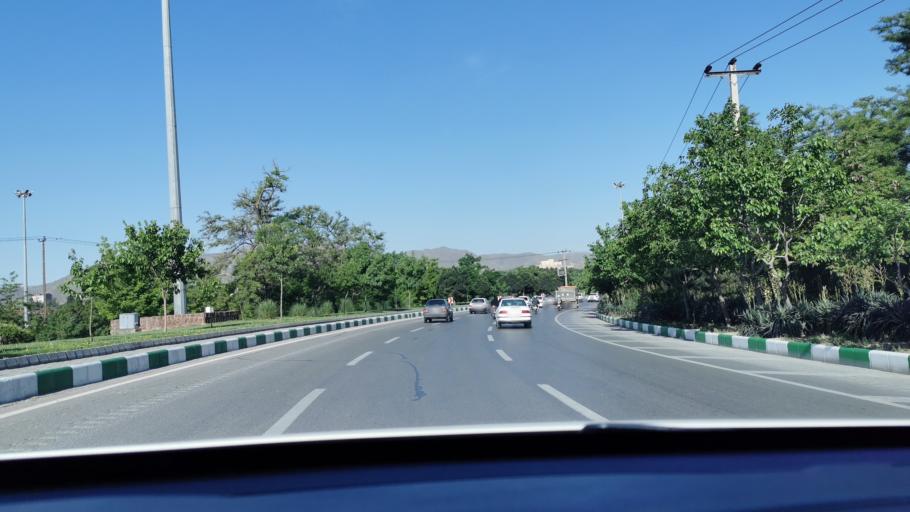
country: IR
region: Razavi Khorasan
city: Mashhad
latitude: 36.2509
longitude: 59.6112
